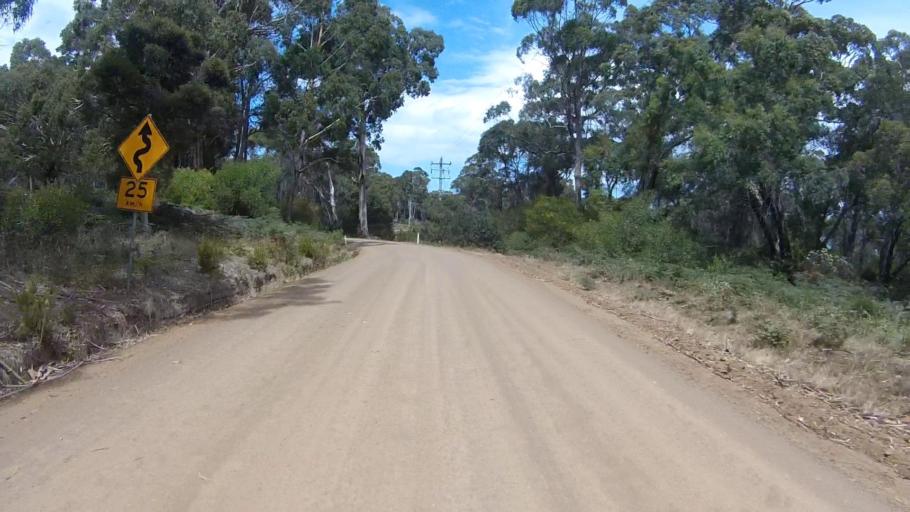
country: AU
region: Tasmania
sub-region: Kingborough
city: Blackmans Bay
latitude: -43.0450
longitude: 147.3064
